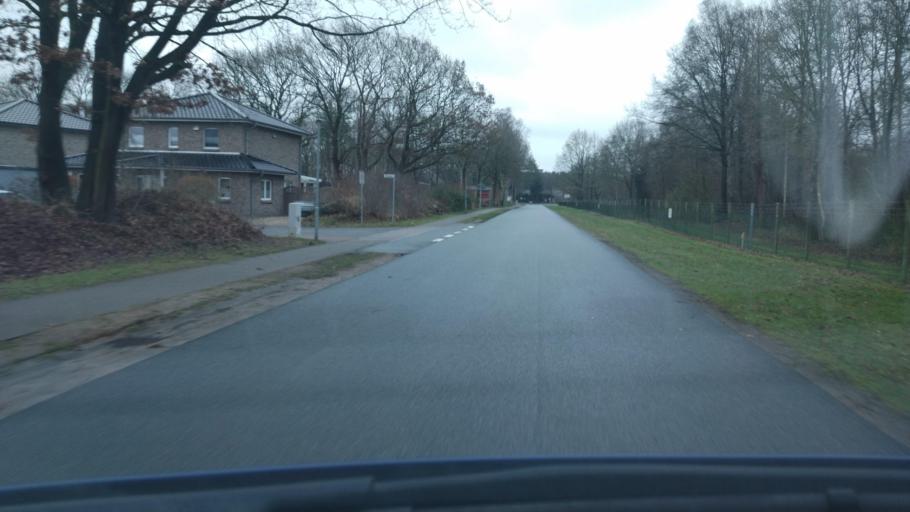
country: DE
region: Schleswig-Holstein
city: Kropp
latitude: 54.4107
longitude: 9.4973
